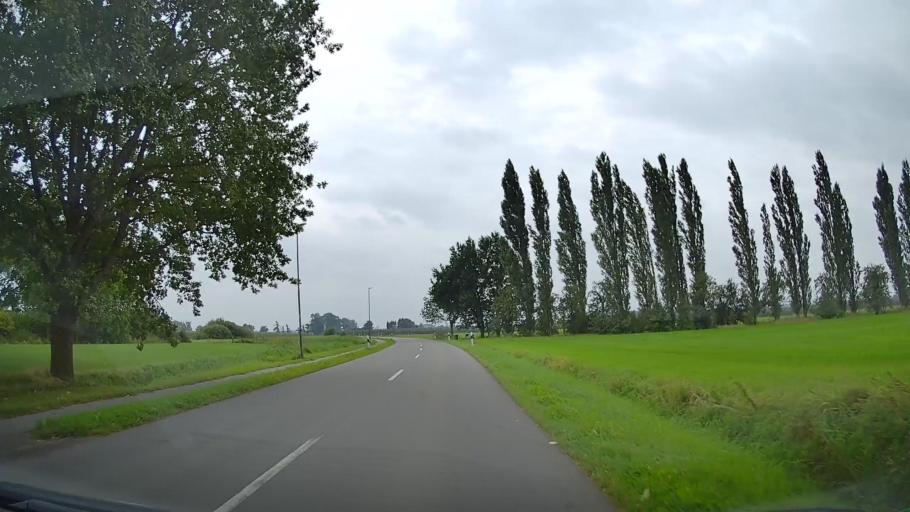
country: DE
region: Lower Saxony
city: Stade
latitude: 53.6335
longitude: 9.4637
